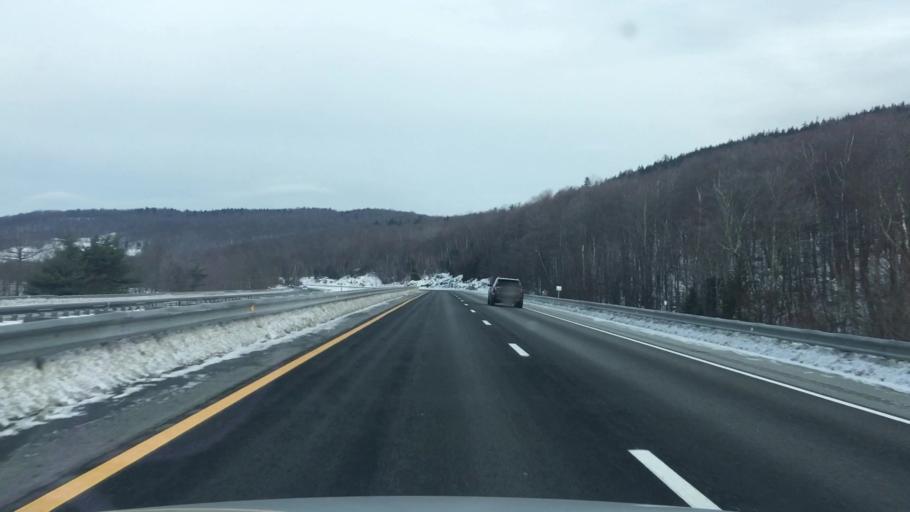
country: US
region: New Hampshire
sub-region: Sullivan County
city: Grantham
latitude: 43.5582
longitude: -72.1418
